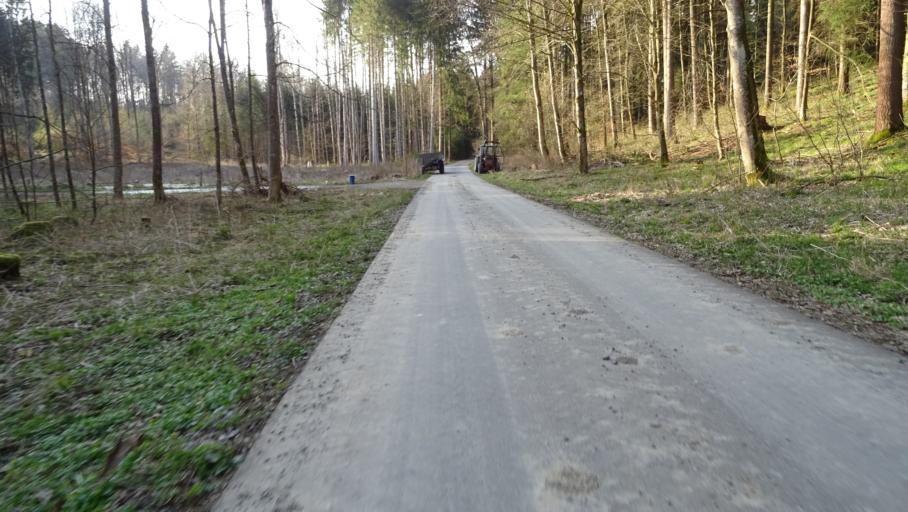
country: DE
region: Baden-Wuerttemberg
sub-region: Regierungsbezirk Stuttgart
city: Roigheim
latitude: 49.3886
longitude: 9.3355
